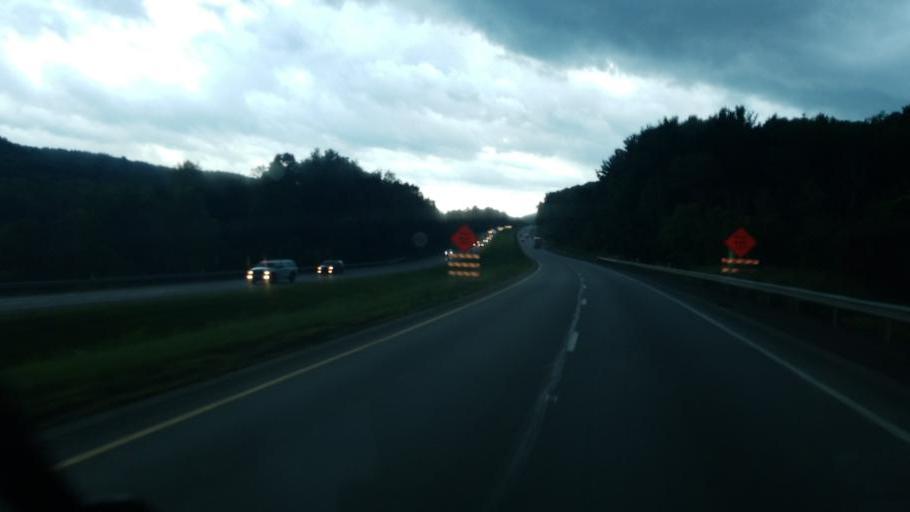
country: US
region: Pennsylvania
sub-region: Butler County
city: Prospect
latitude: 40.8756
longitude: -80.1140
